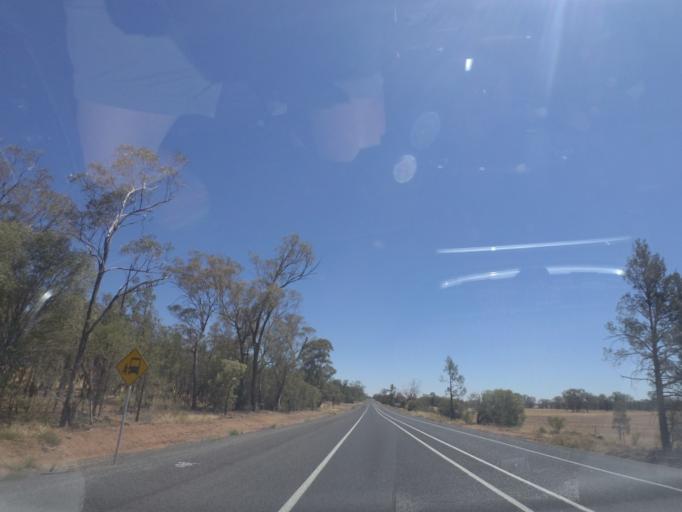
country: AU
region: New South Wales
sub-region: Gilgandra
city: Gilgandra
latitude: -31.4958
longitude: 148.8640
